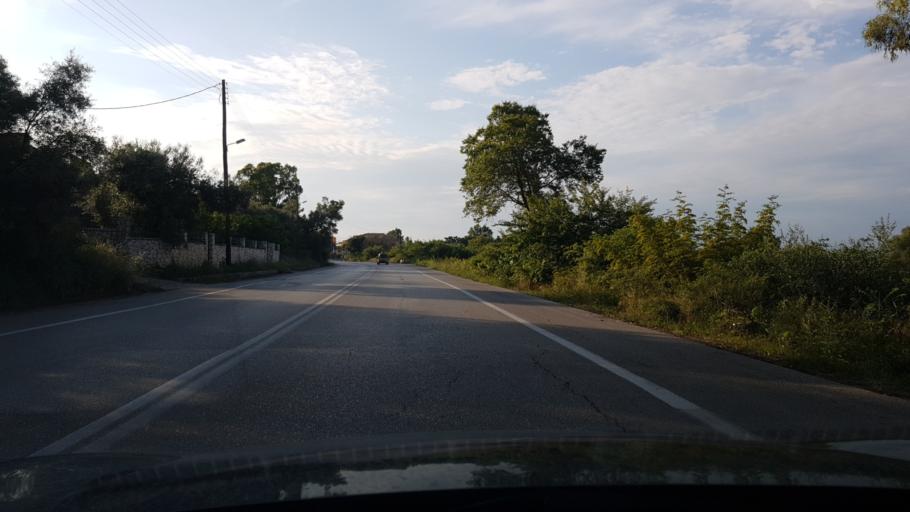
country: GR
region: Ionian Islands
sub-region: Lefkada
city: Lefkada
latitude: 38.8132
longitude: 20.7144
